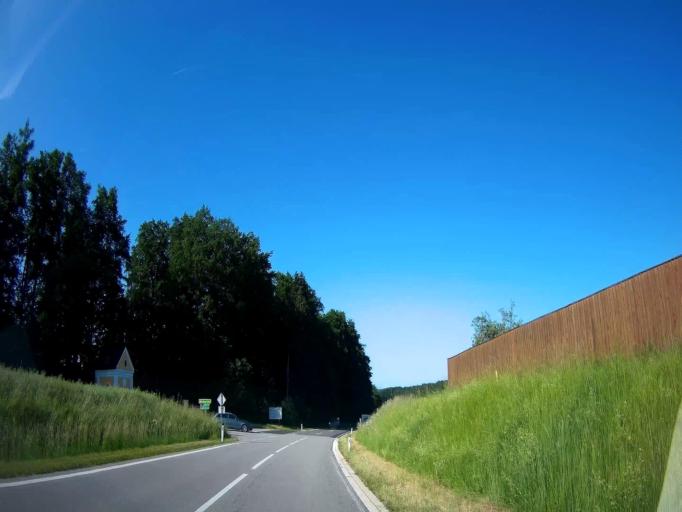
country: AT
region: Salzburg
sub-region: Politischer Bezirk Salzburg-Umgebung
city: Dorfbeuern
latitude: 48.0989
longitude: 12.9910
